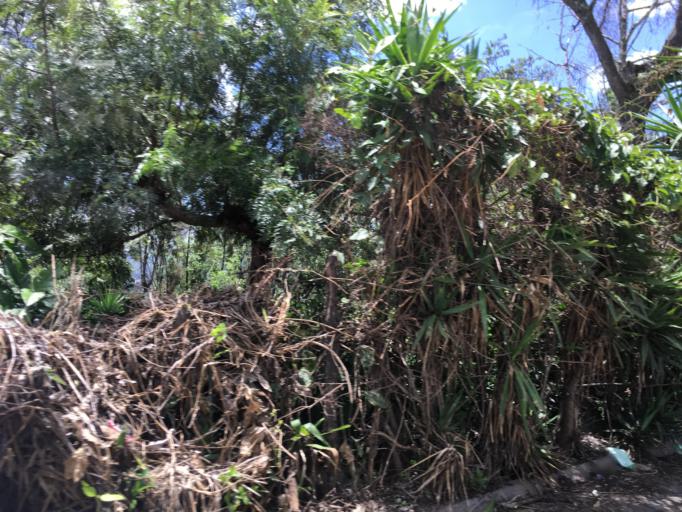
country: GT
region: Sacatepequez
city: Ciudad Vieja
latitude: 14.5238
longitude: -90.7469
